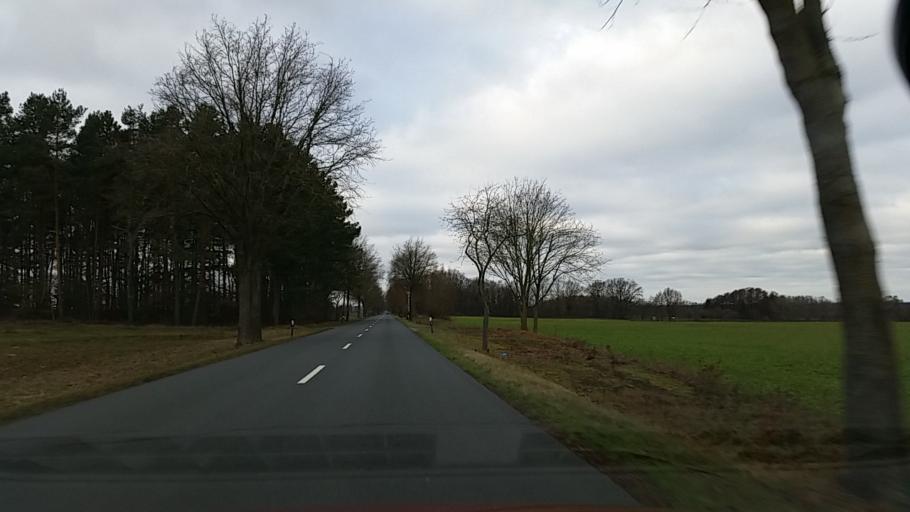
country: DE
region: Lower Saxony
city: Wrestedt
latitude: 52.8827
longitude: 10.6066
